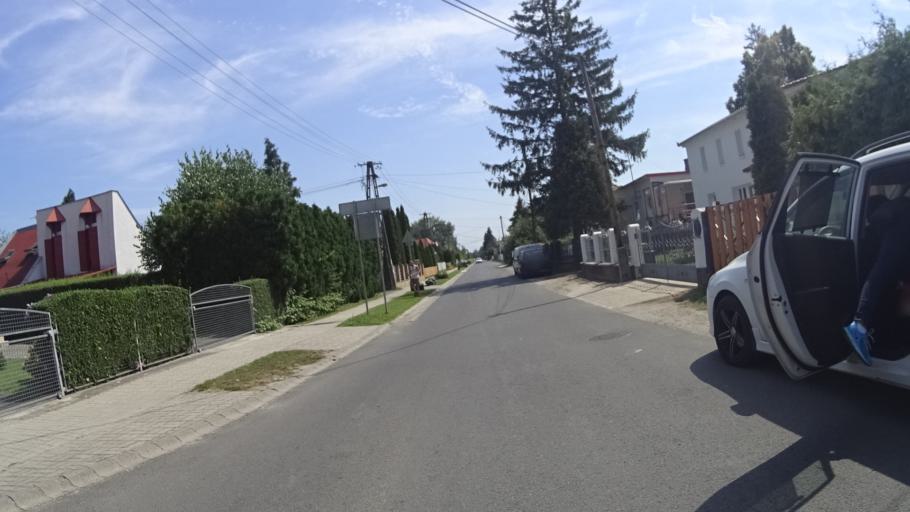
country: HU
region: Somogy
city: Kethely
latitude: 46.7043
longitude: 17.3820
